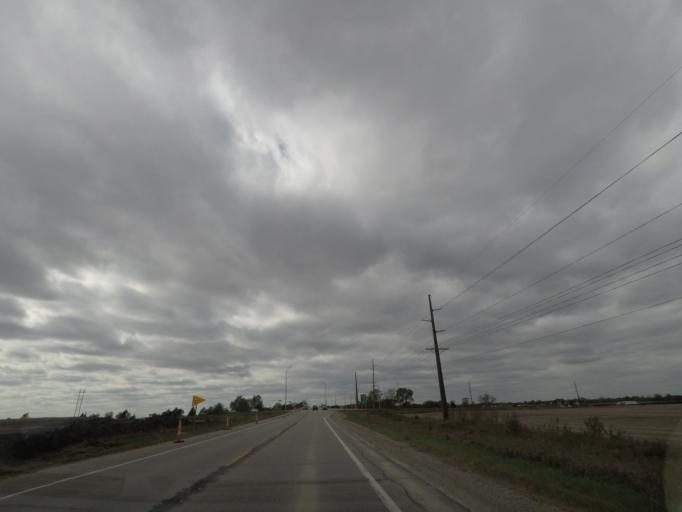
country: US
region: Iowa
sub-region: Story County
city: Huxley
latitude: 41.8778
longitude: -93.5668
